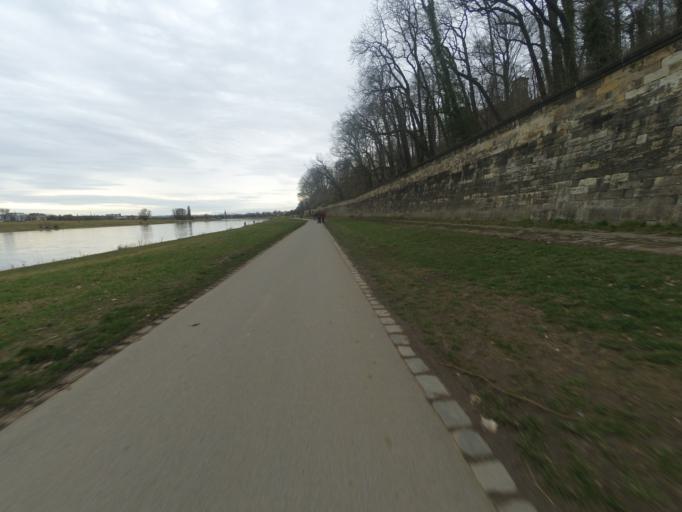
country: DE
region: Saxony
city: Albertstadt
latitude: 51.0633
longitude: 13.7964
